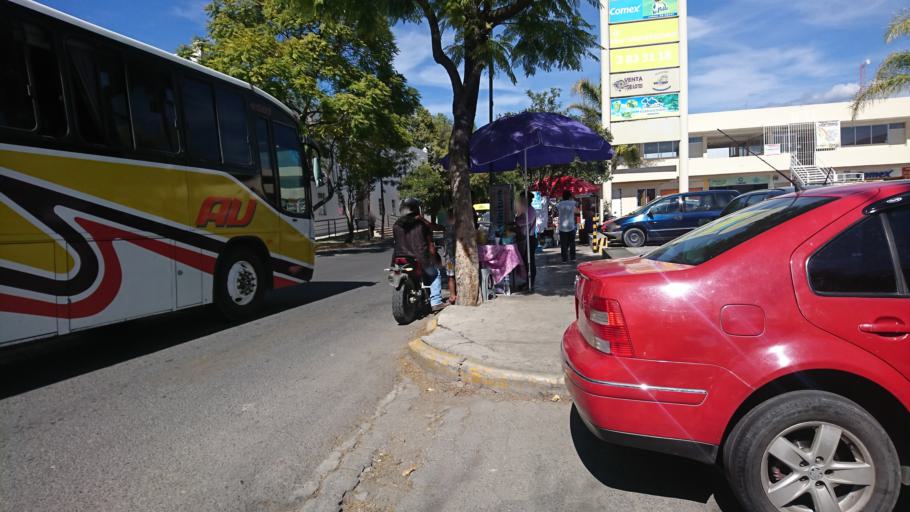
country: MX
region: Puebla
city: Tehuacan
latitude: 18.4697
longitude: -97.3928
